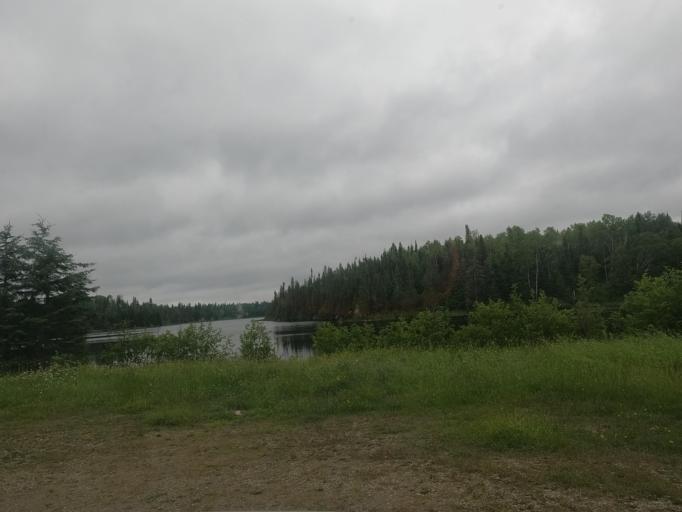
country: CA
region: Ontario
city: Hearst
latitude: 49.7983
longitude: -83.9863
